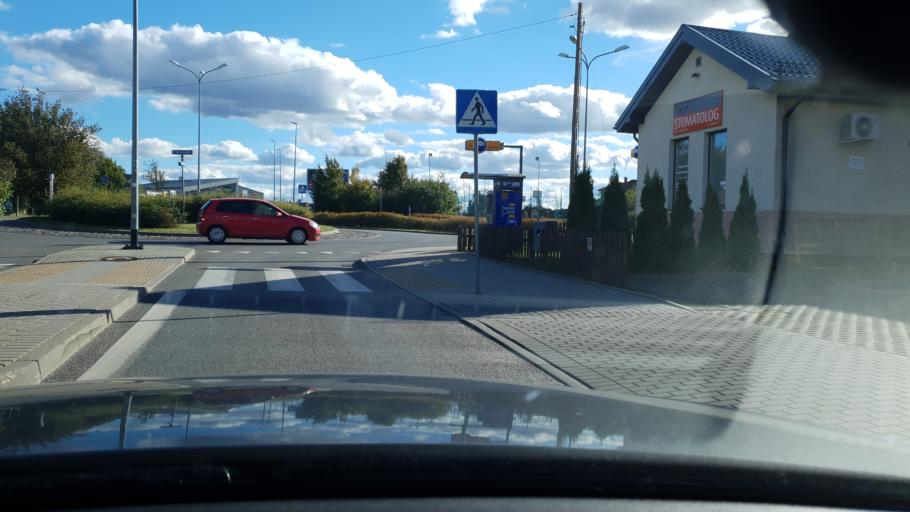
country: PL
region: Pomeranian Voivodeship
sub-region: Powiat kartuski
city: Chwaszczyno
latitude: 54.4987
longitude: 18.4384
